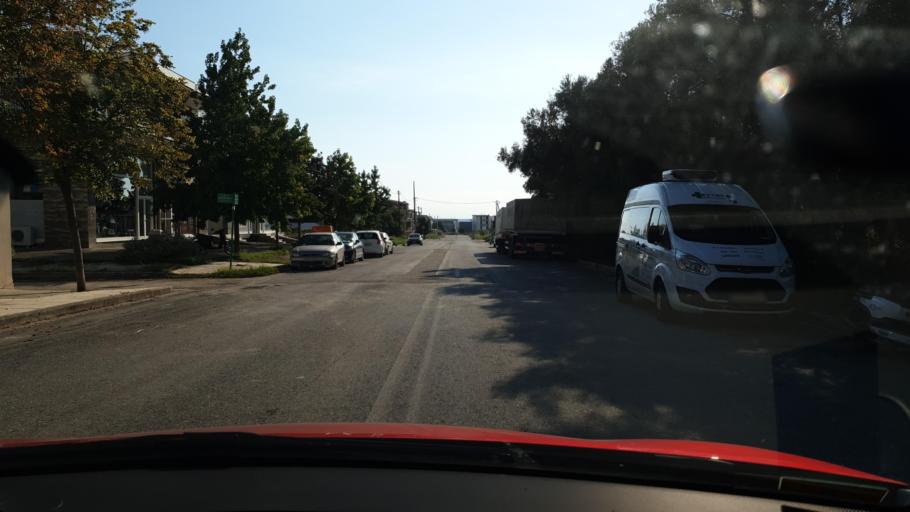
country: GR
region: Central Macedonia
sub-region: Nomos Thessalonikis
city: Thermi
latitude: 40.5437
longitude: 23.0161
